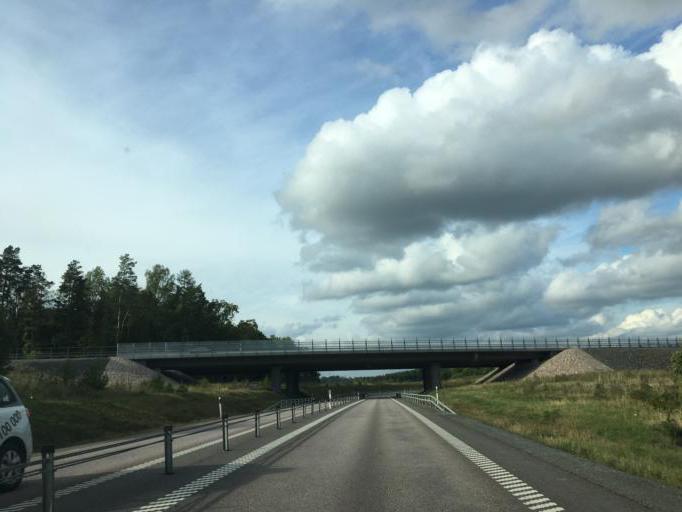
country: SE
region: Uppsala
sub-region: Enkopings Kommun
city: Enkoping
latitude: 59.6439
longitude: 17.0531
